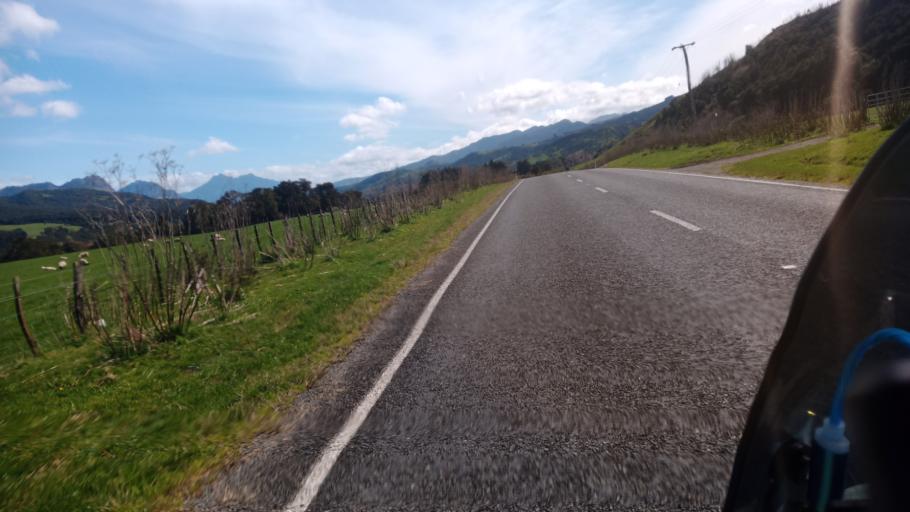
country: NZ
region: Gisborne
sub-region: Gisborne District
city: Gisborne
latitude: -37.8740
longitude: 178.2806
